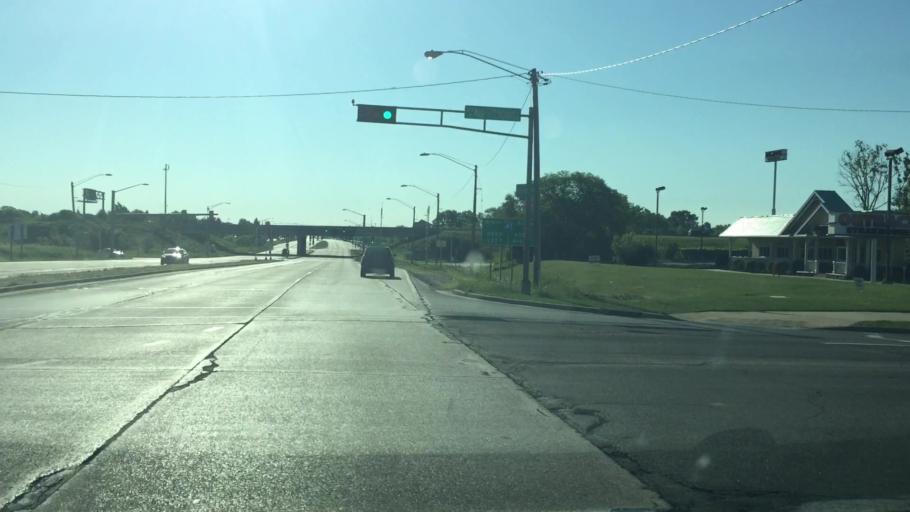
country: US
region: Wisconsin
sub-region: Outagamie County
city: Appleton
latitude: 44.2619
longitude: -88.4694
